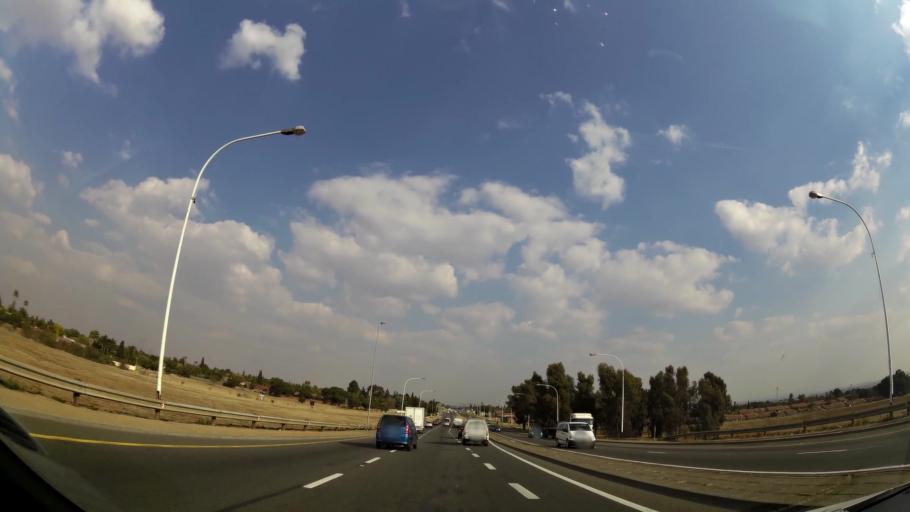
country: ZA
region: Gauteng
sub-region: Ekurhuleni Metropolitan Municipality
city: Boksburg
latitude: -26.2530
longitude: 28.2446
